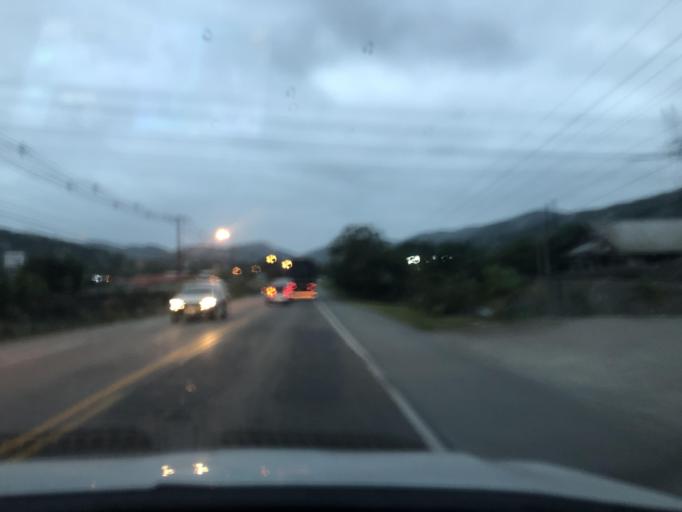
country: BR
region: Santa Catarina
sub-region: Pomerode
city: Pomerode
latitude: -26.7802
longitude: -49.0836
